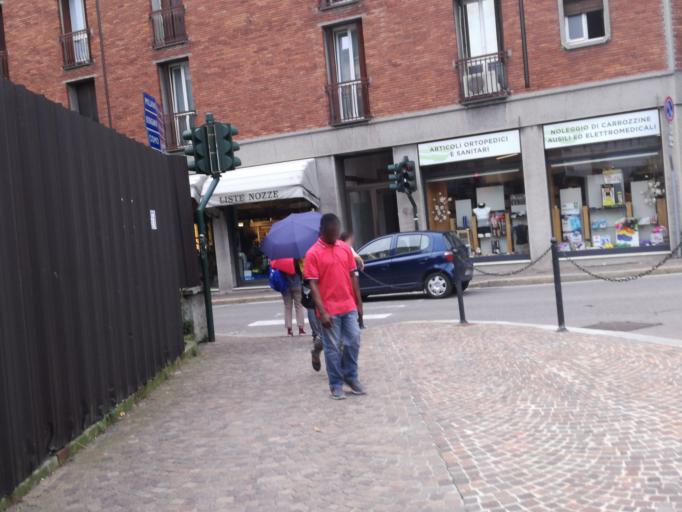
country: IT
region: Lombardy
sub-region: Provincia di Lecco
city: Lecco
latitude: 45.8506
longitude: 9.3963
